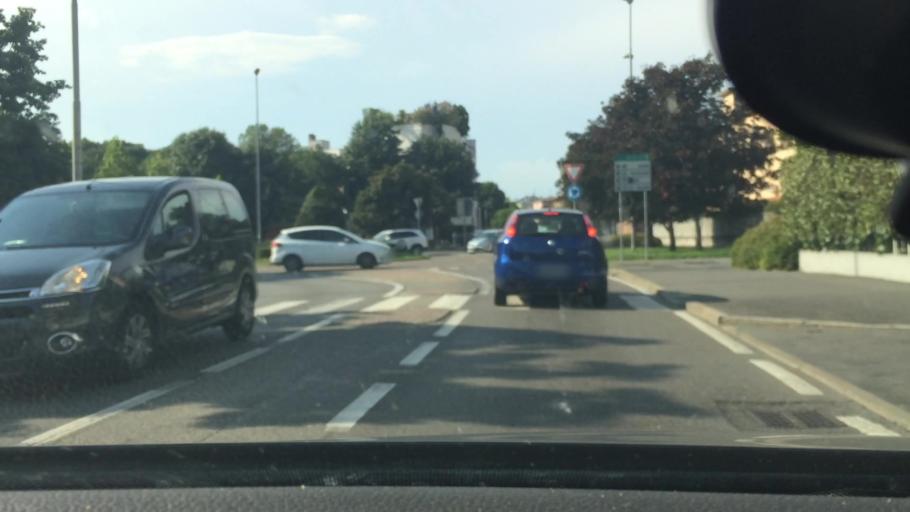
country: IT
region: Lombardy
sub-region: Citta metropolitana di Milano
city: Settimo Milanese
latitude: 45.4863
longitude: 9.0570
